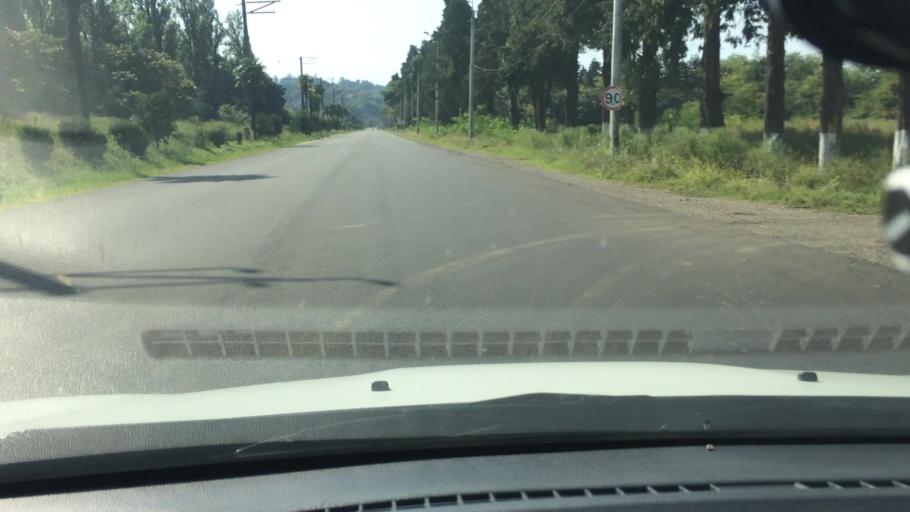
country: GE
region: Ajaria
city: Kobuleti
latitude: 41.7885
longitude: 41.7670
